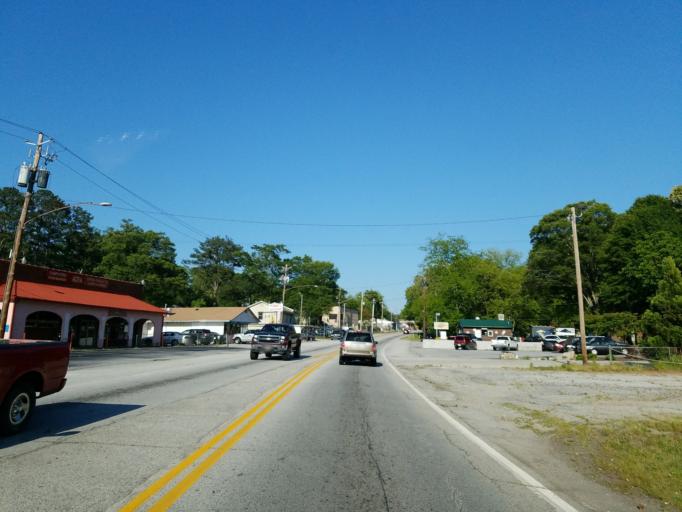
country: US
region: Georgia
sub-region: Carroll County
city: Villa Rica
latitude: 33.7327
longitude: -84.9254
